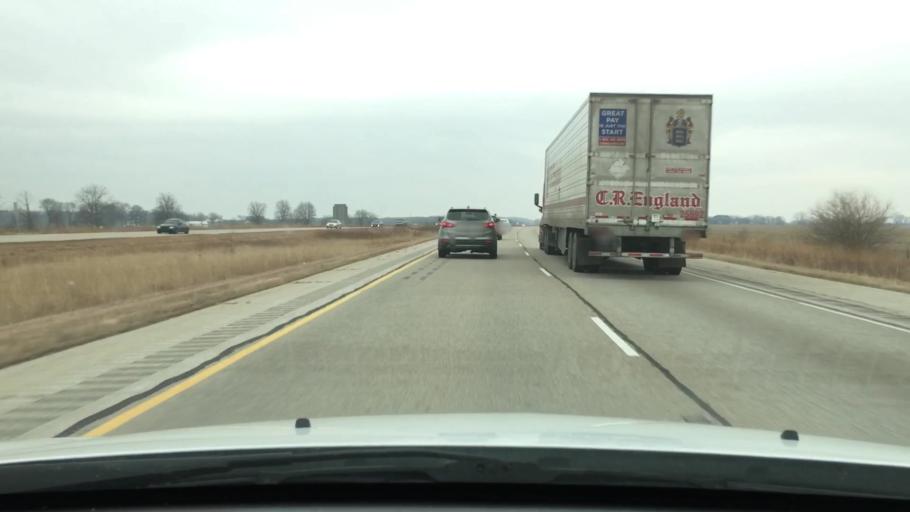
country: US
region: Illinois
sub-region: Logan County
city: Atlanta
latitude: 40.3283
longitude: -89.1522
